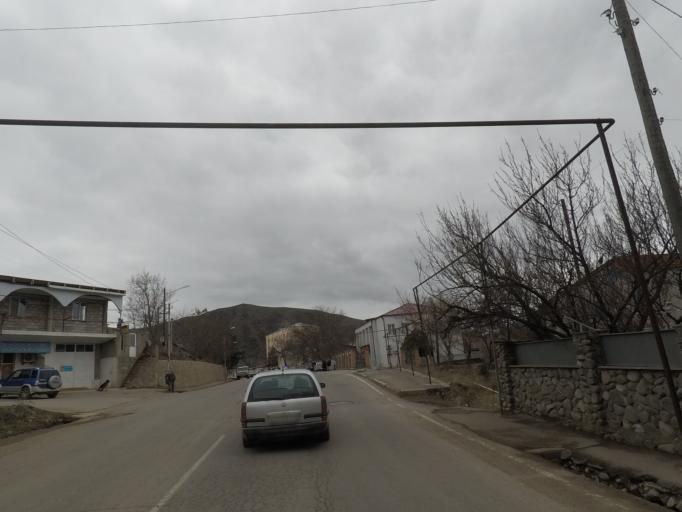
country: GE
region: Samtskhe-Javakheti
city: Aspindza
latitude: 41.5702
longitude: 43.2541
